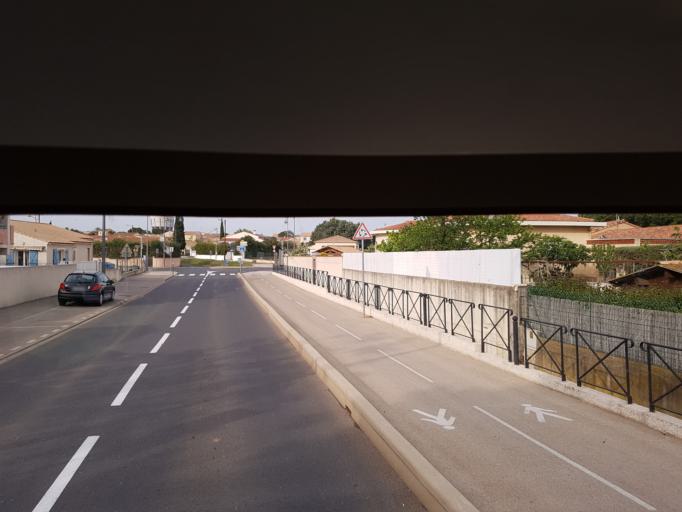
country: FR
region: Languedoc-Roussillon
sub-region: Departement de l'Herault
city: Marseillan
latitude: 43.3599
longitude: 3.5242
